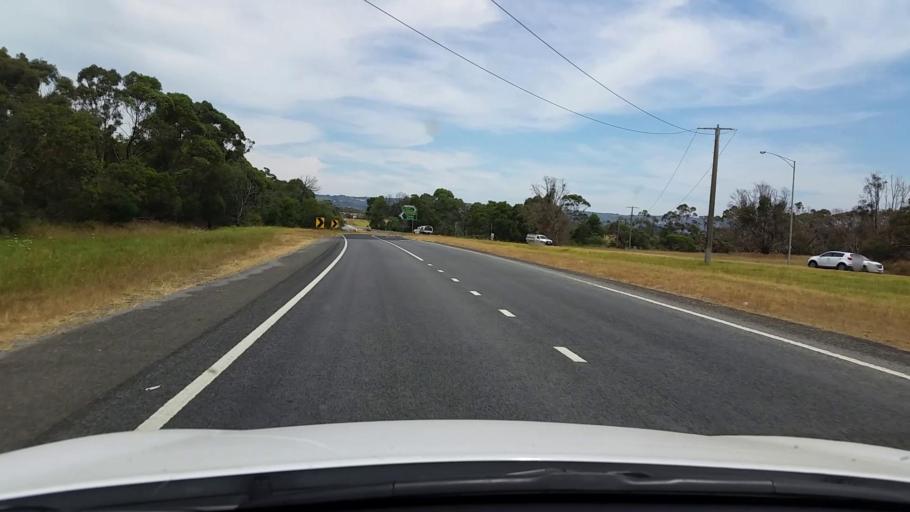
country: AU
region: Victoria
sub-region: Mornington Peninsula
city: Safety Beach
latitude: -38.3031
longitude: 145.0322
